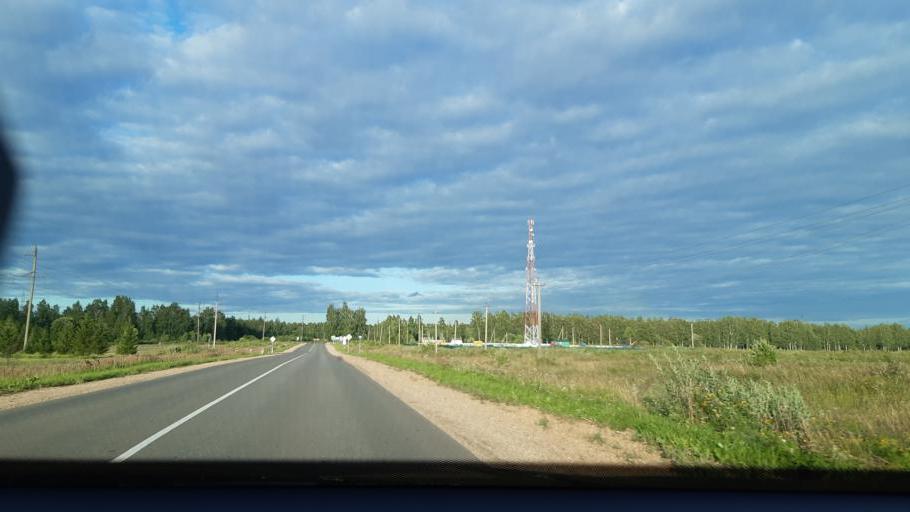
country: RU
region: Smolensk
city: Yel'nya
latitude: 54.5943
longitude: 33.1833
